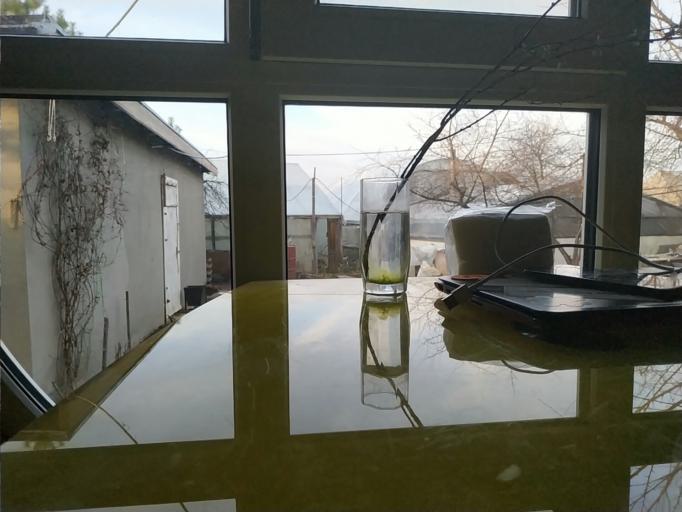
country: RU
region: Republic of Karelia
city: Suoyarvi
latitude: 62.2841
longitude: 32.0798
